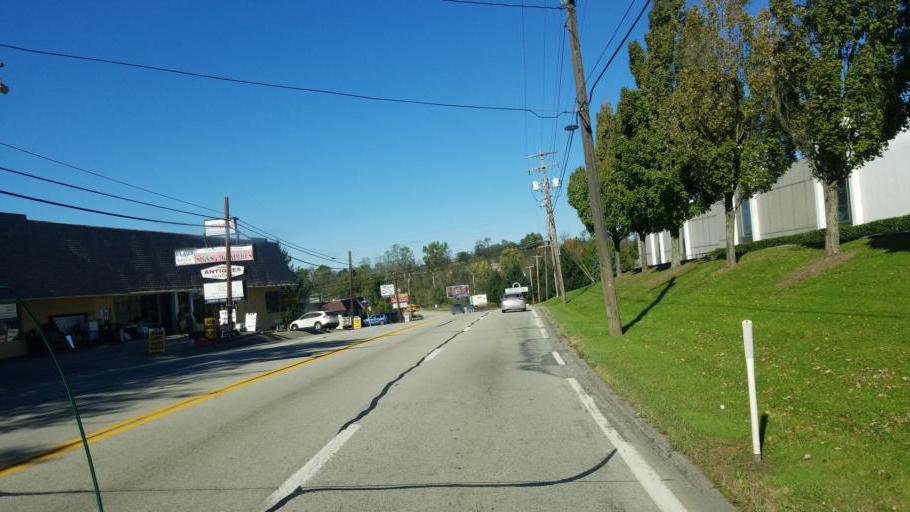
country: US
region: Pennsylvania
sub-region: Westmoreland County
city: Trafford
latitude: 40.3582
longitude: -79.7704
